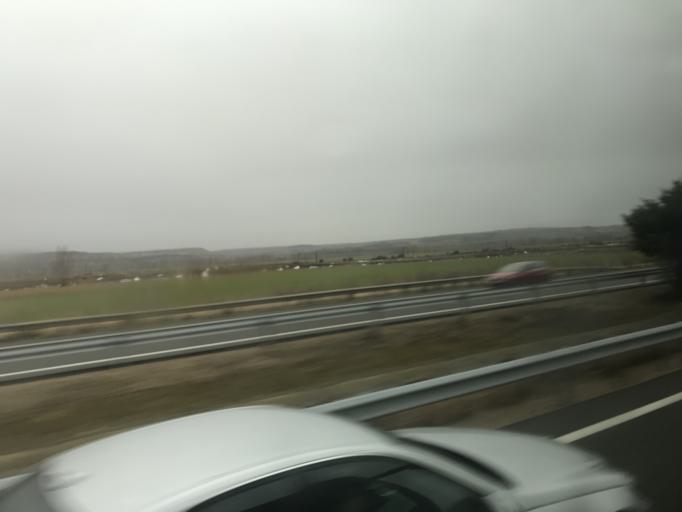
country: ES
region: Castille and Leon
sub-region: Provincia de Burgos
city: Villazopeque
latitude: 42.1941
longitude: -4.0293
